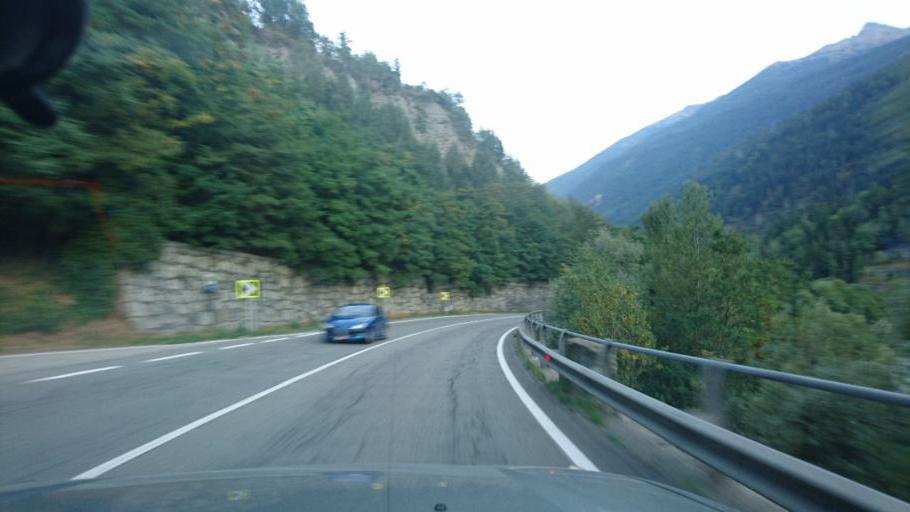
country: IT
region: Aosta Valley
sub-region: Valle d'Aosta
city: La Salle
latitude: 45.7407
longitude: 7.0680
